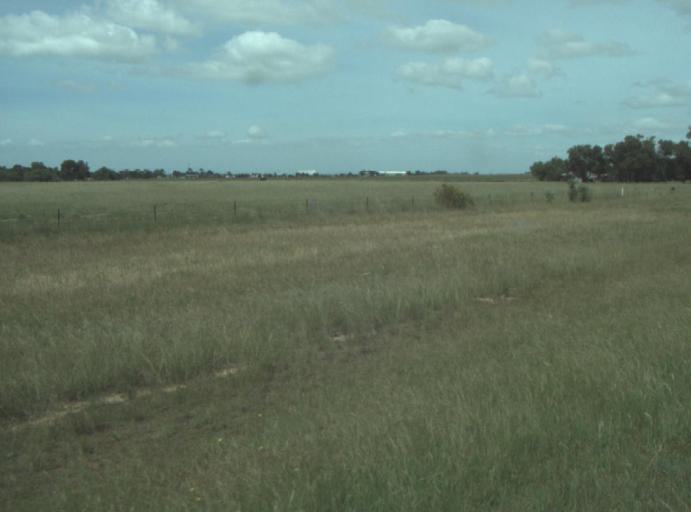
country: AU
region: Victoria
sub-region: Wyndham
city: Little River
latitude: -37.9868
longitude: 144.4943
